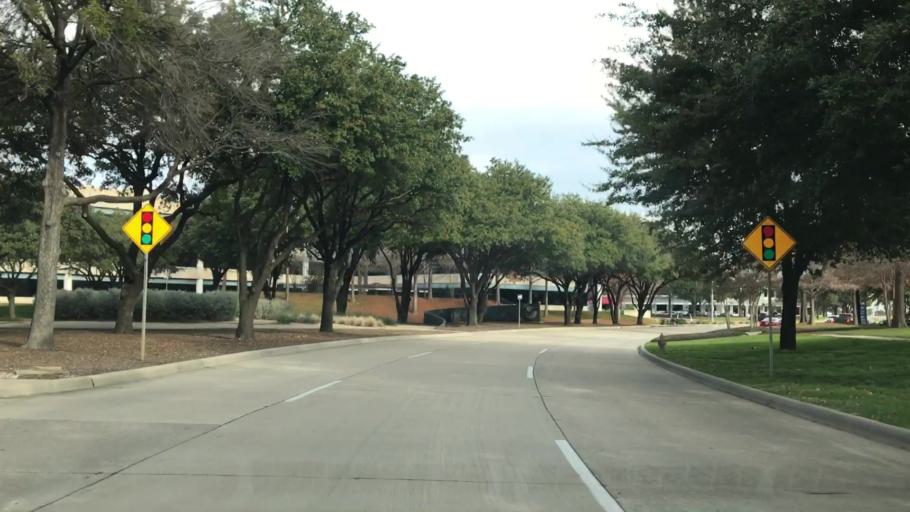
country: US
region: Texas
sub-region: Dallas County
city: Coppell
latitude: 32.9271
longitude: -97.0117
